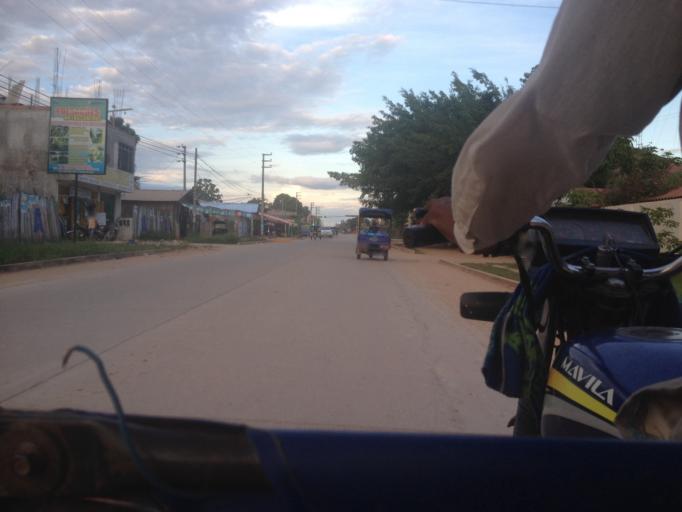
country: PE
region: Ucayali
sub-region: Provincia de Coronel Portillo
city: Pucallpa
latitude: -8.3817
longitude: -74.5626
